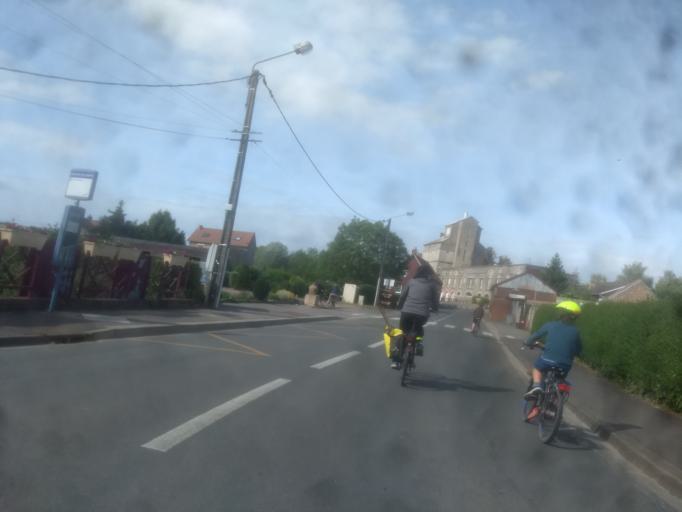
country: FR
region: Nord-Pas-de-Calais
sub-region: Departement du Pas-de-Calais
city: Feuchy
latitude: 50.2968
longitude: 2.8378
